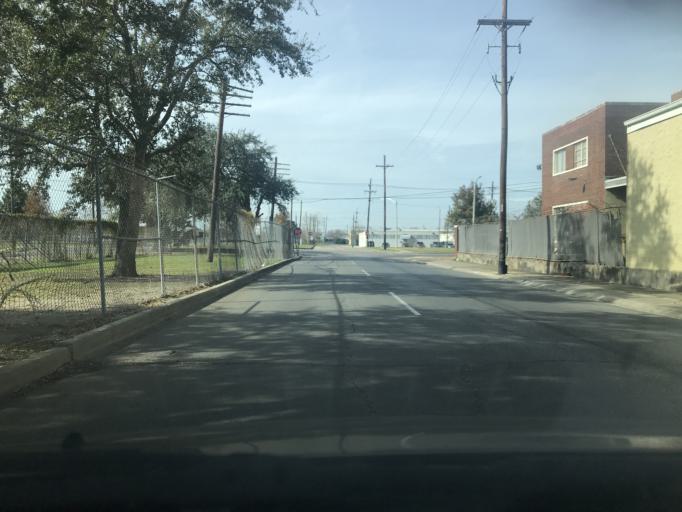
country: US
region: Louisiana
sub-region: Orleans Parish
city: New Orleans
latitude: 29.9587
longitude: -90.1025
